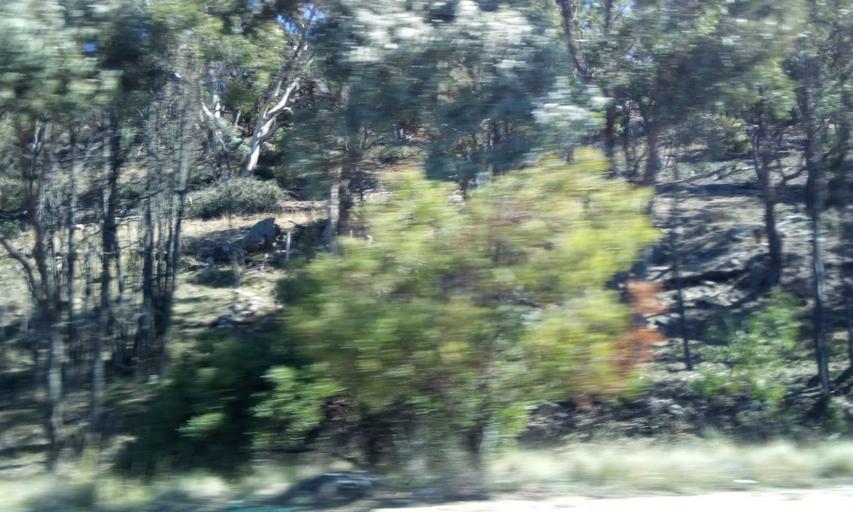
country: AU
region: New South Wales
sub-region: Yass Valley
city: Gundaroo
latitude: -35.0954
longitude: 149.3762
